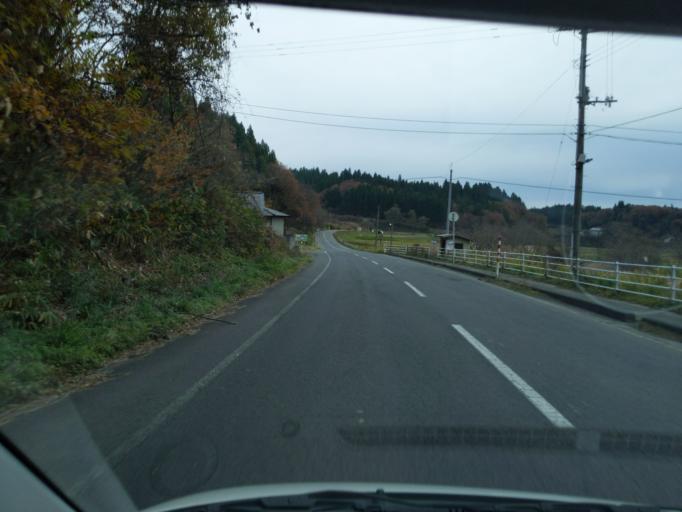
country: JP
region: Iwate
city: Kitakami
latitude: 39.2651
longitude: 141.2682
